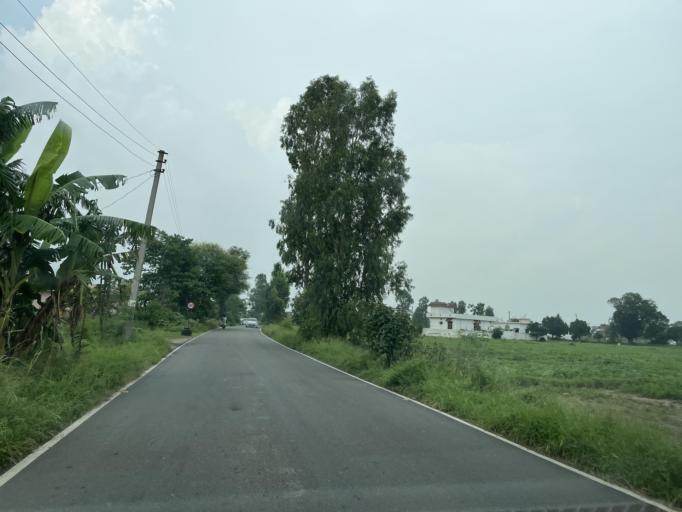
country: IN
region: Uttarakhand
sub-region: Naini Tal
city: Haldwani
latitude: 29.1766
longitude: 79.4711
